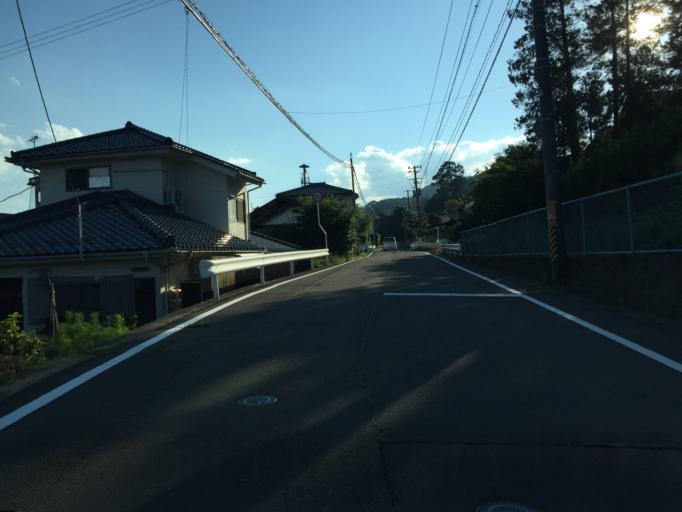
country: JP
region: Fukushima
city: Hobaramachi
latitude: 37.8382
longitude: 140.4996
